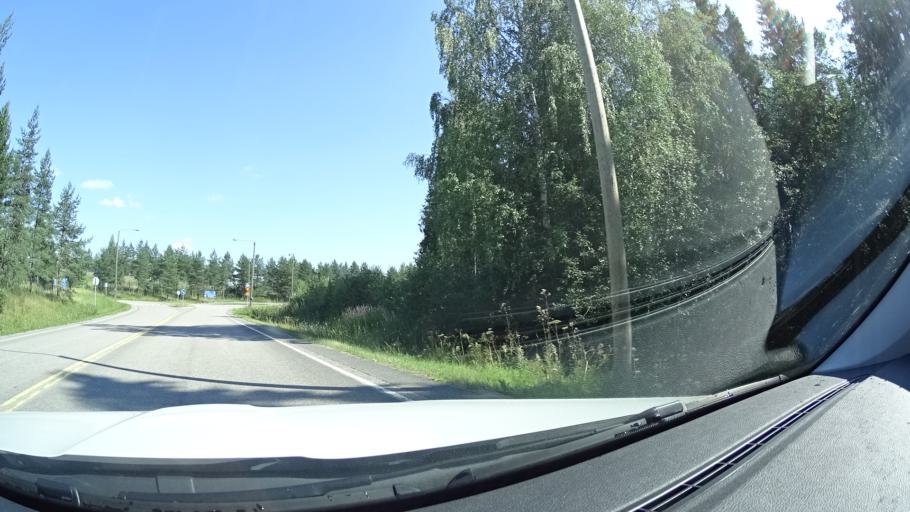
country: FI
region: Uusimaa
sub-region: Helsinki
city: Nurmijaervi
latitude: 60.3540
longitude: 24.8049
